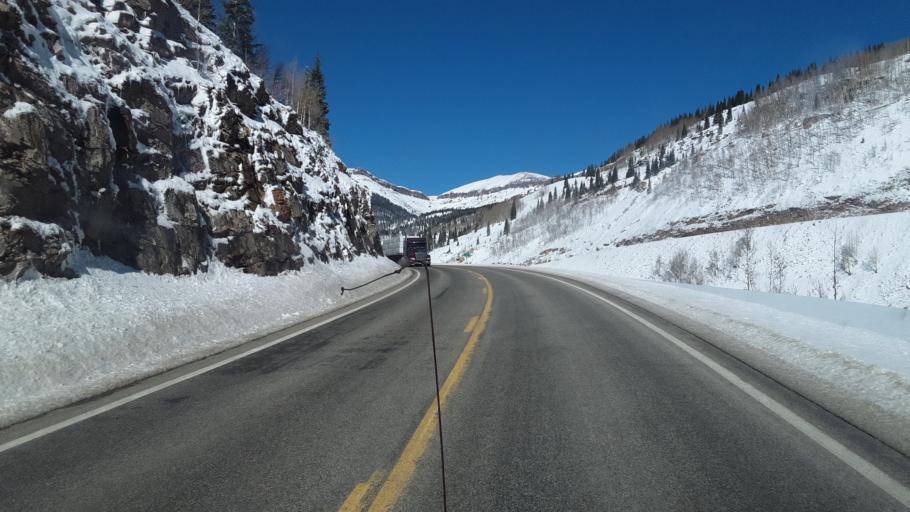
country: US
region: Colorado
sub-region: San Juan County
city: Silverton
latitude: 37.7255
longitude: -107.7495
